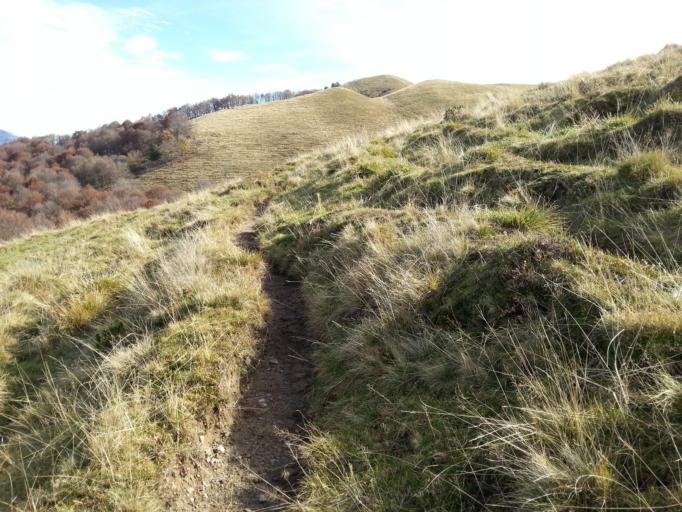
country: IT
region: Lombardy
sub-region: Provincia di Bergamo
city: Fuipiano Valle Imagna
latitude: 45.8698
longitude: 9.5156
